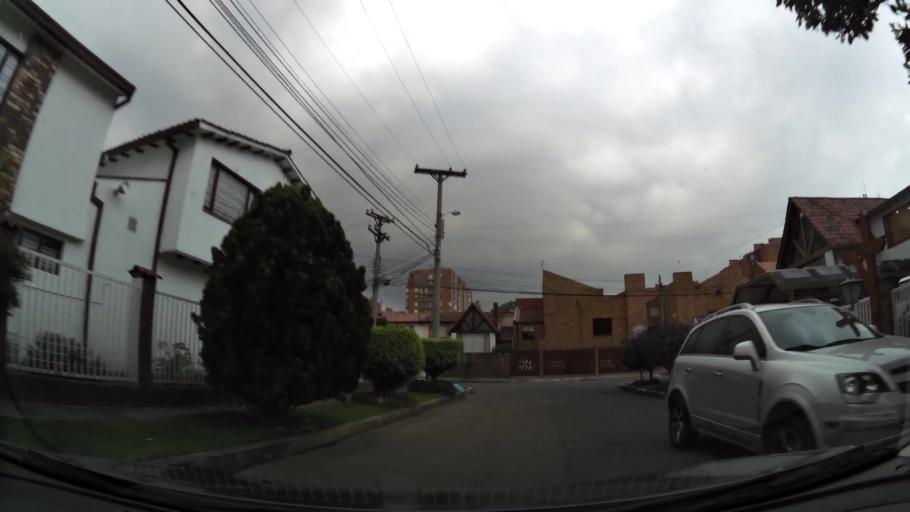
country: CO
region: Bogota D.C.
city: Barrio San Luis
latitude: 4.7256
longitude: -74.0644
